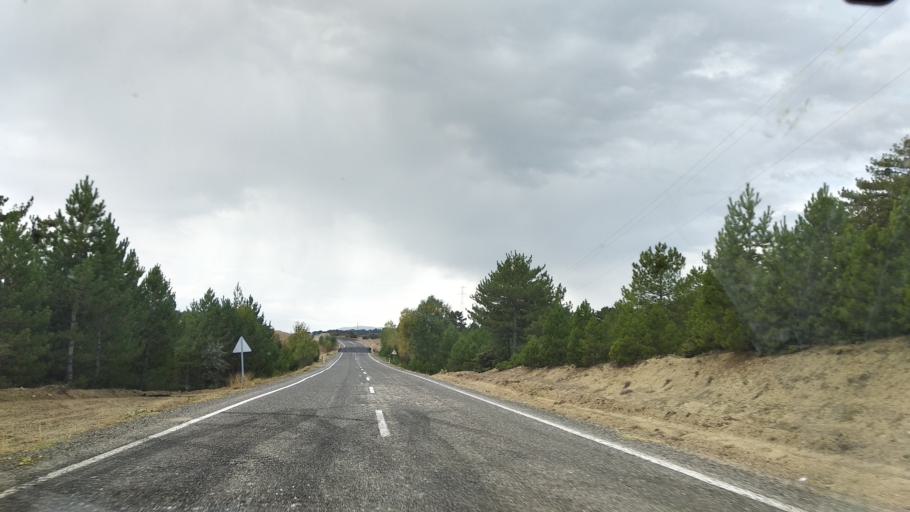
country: TR
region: Bolu
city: Seben
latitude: 40.3524
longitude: 31.4811
